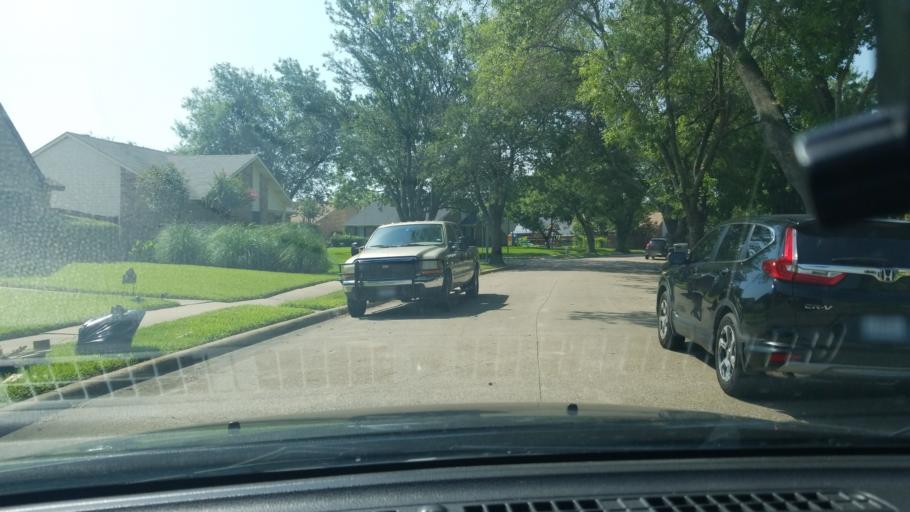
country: US
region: Texas
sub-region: Dallas County
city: Mesquite
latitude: 32.8223
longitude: -96.6238
